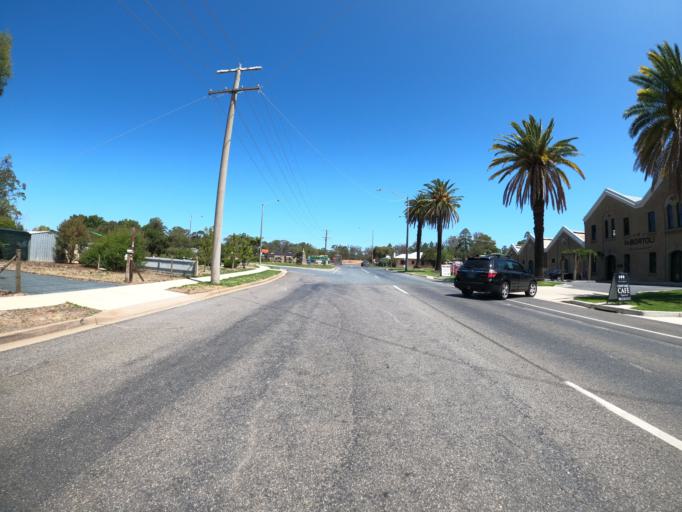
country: AU
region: New South Wales
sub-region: Corowa Shire
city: Corowa
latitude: -36.0517
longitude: 146.4551
